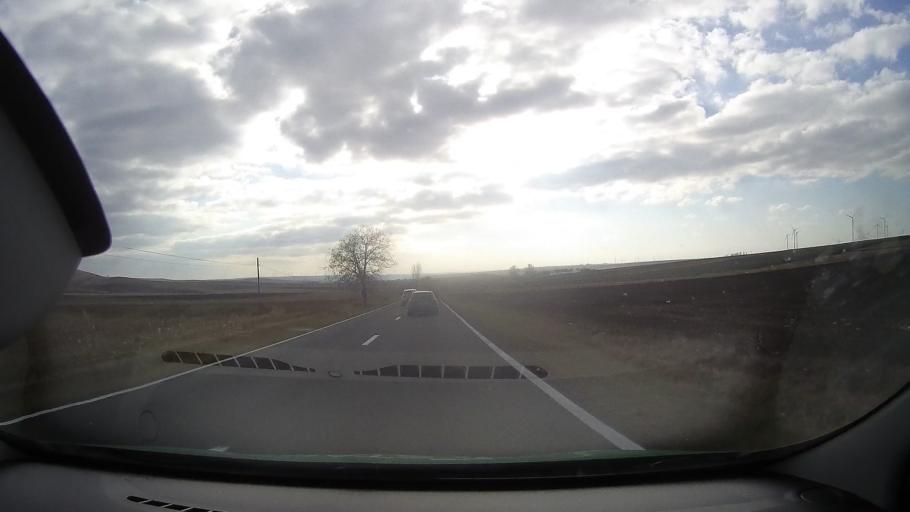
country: RO
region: Tulcea
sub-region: Comuna Topolog
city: Topolog
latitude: 44.8925
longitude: 28.3950
